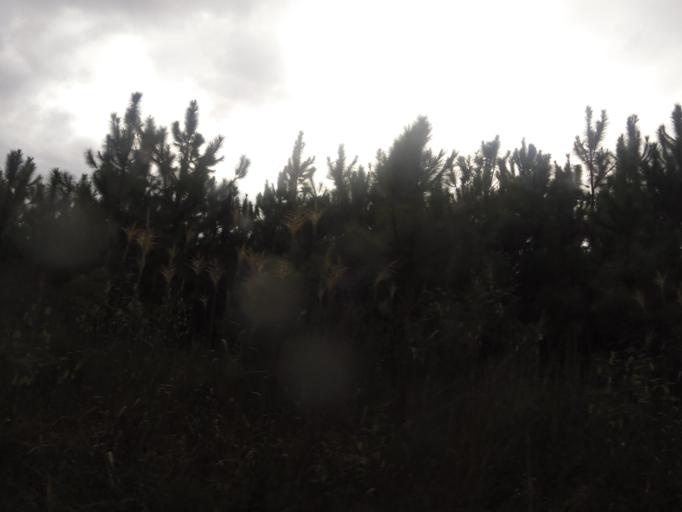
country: US
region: Florida
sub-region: Flagler County
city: Bunnell
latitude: 29.5476
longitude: -81.3261
